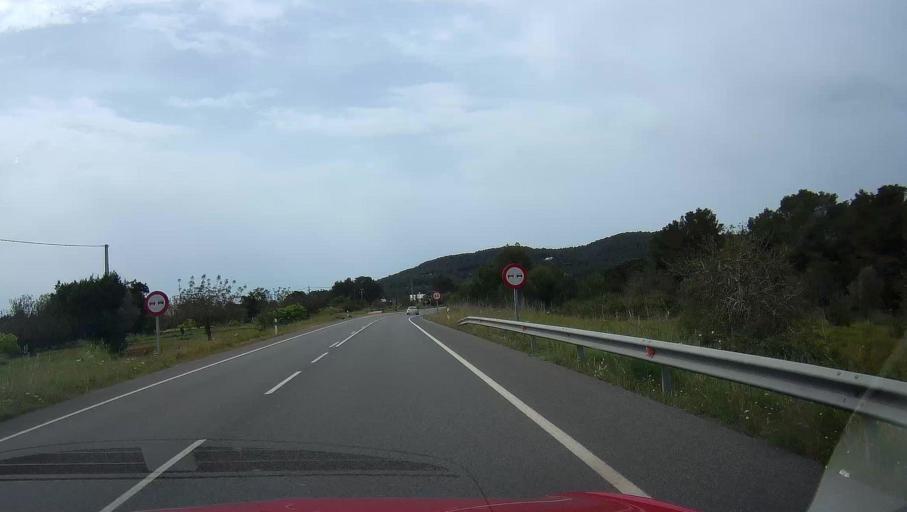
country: ES
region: Balearic Islands
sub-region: Illes Balears
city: Sant Joan de Labritja
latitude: 39.0546
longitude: 1.4929
